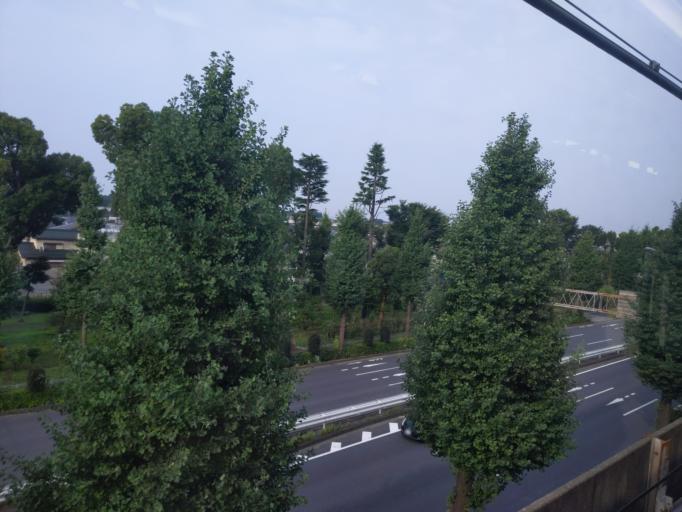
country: JP
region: Saitama
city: Wako
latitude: 35.7913
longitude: 139.6488
